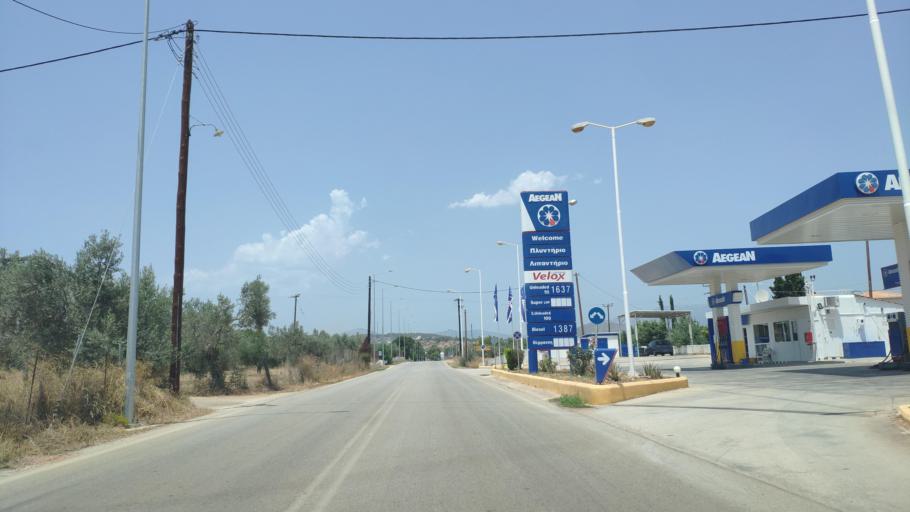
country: GR
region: Peloponnese
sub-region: Nomos Argolidos
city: Porto Cheli
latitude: 37.3435
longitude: 23.1576
